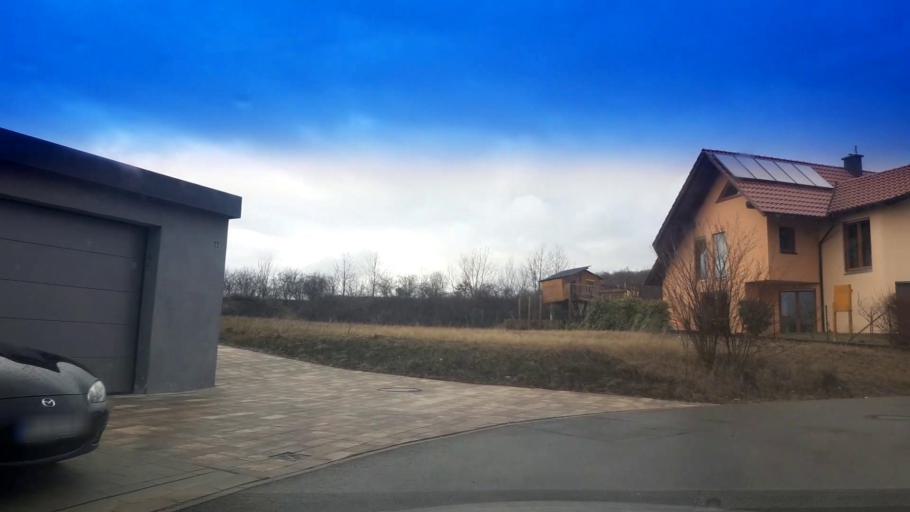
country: DE
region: Bavaria
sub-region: Upper Franconia
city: Litzendorf
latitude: 49.8707
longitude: 11.0222
